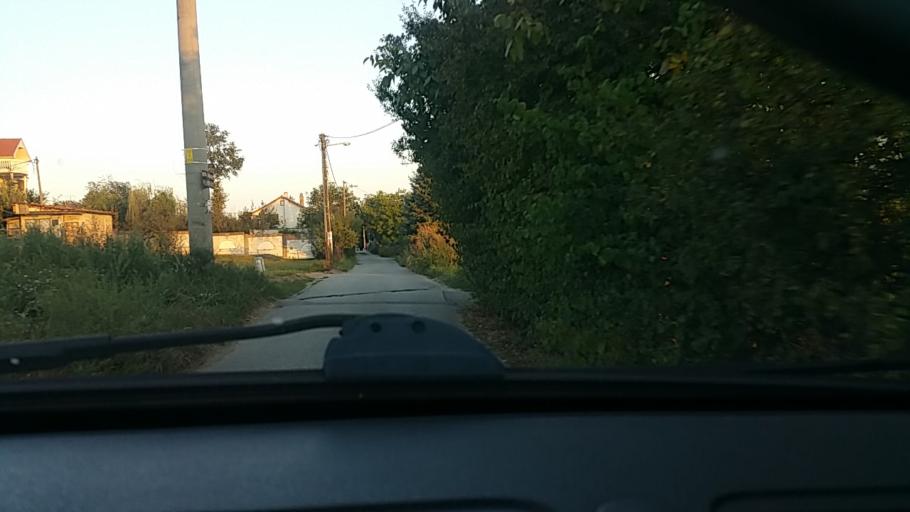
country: RS
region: Central Serbia
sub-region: Belgrade
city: Rakovica
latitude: 44.7331
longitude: 20.4644
